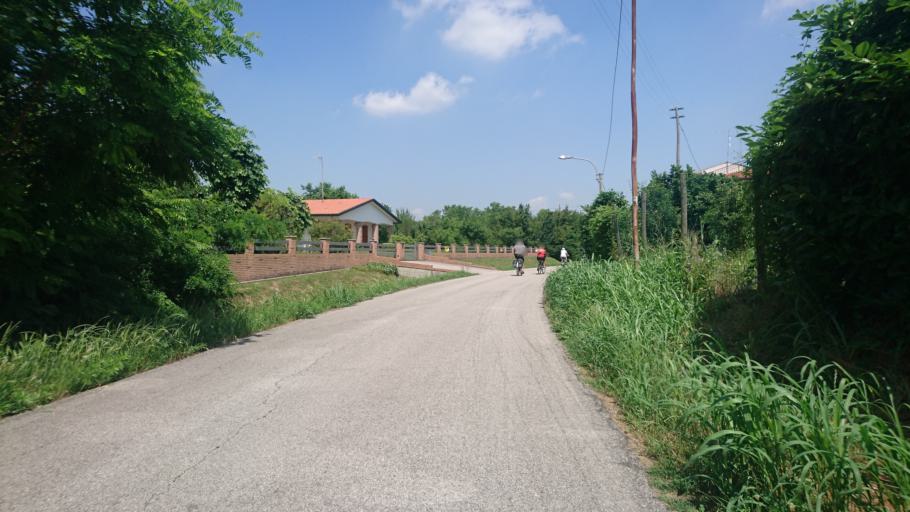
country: IT
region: Veneto
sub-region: Provincia di Venezia
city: Galta
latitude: 45.3972
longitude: 12.0190
